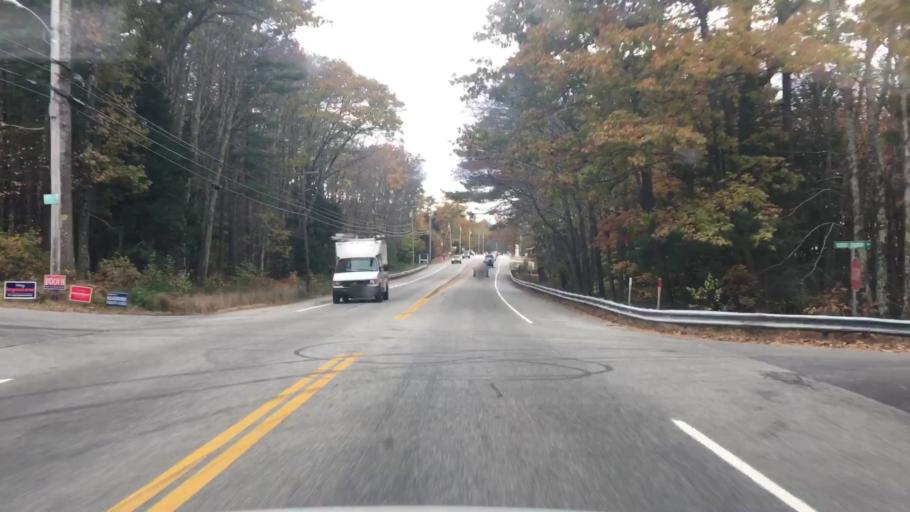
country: US
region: Maine
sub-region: York County
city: West Kennebunk
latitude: 43.4784
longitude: -70.5833
